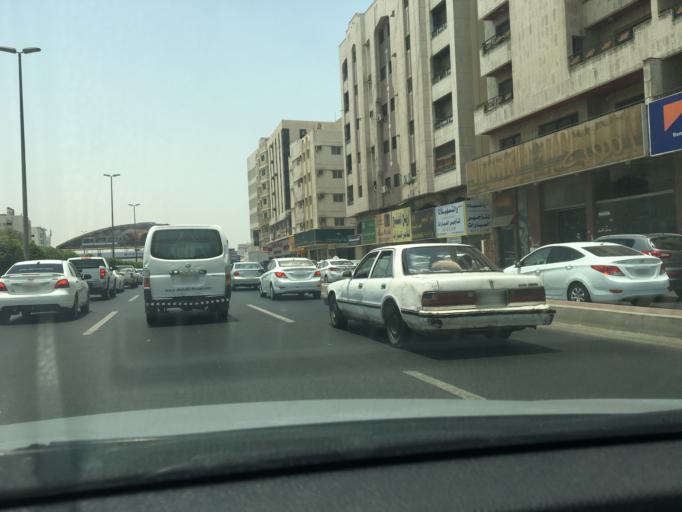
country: SA
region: Makkah
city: Jeddah
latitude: 21.5367
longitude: 39.1921
